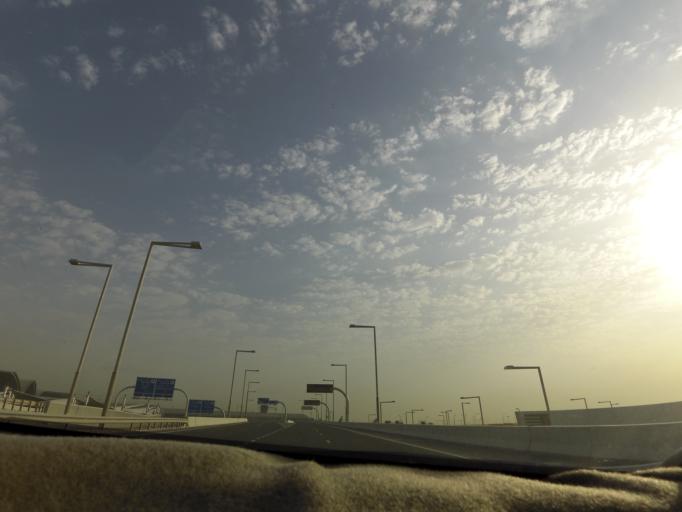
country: QA
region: Al Wakrah
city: Al Wakrah
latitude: 25.2577
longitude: 51.6170
